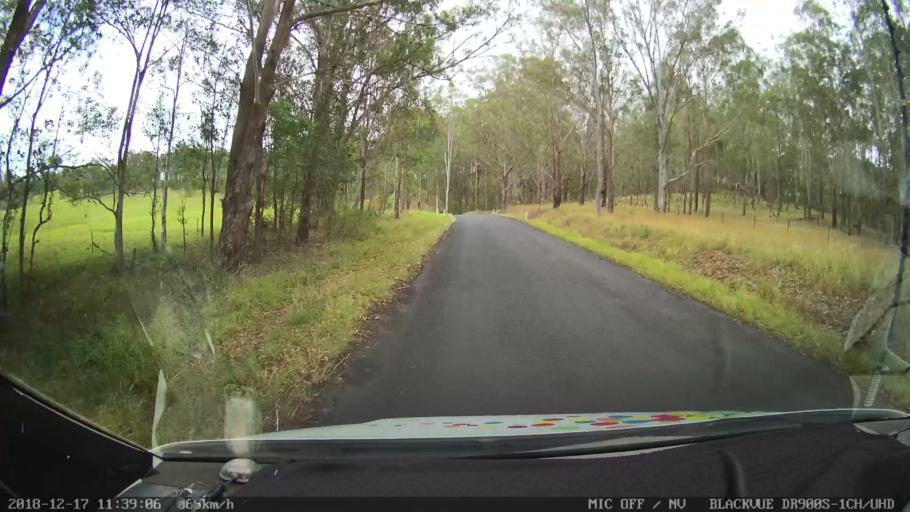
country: AU
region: New South Wales
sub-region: Kyogle
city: Kyogle
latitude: -28.6897
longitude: 152.5965
